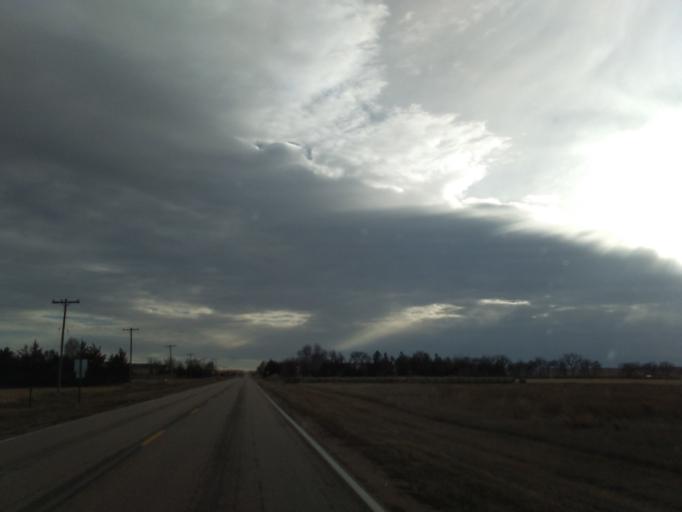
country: US
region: Nebraska
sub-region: Morrill County
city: Bridgeport
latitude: 41.6546
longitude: -103.0995
